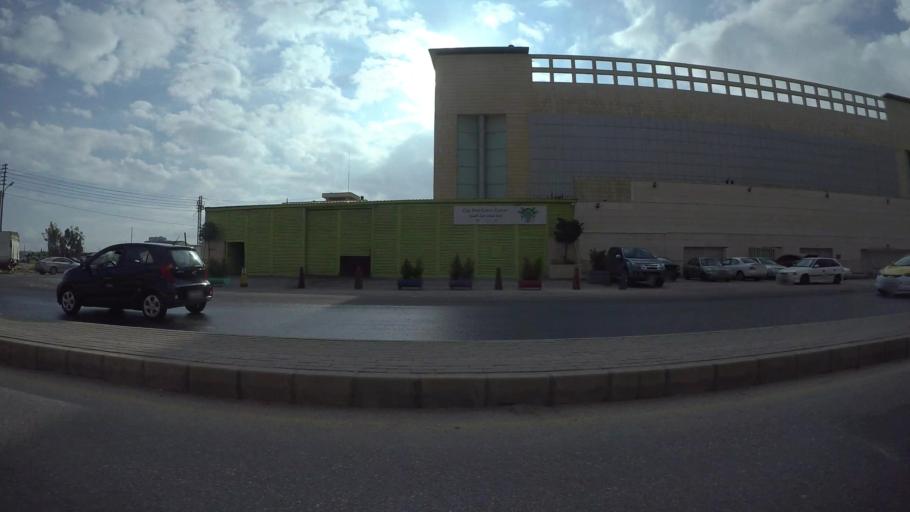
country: JO
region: Amman
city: Wadi as Sir
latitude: 31.9807
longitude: 35.8396
